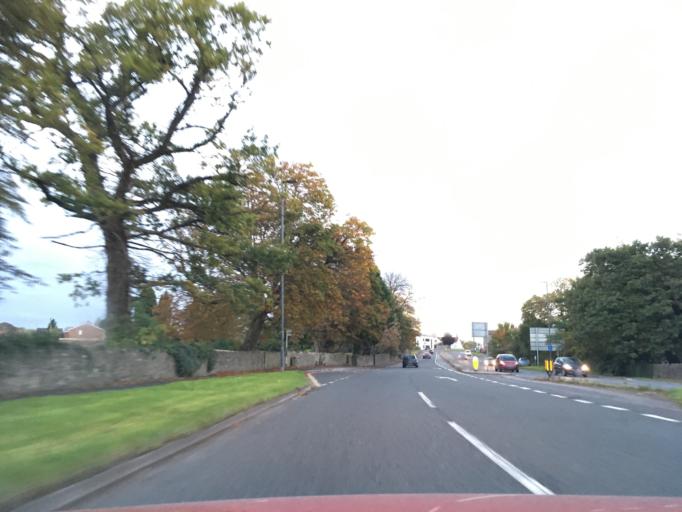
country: GB
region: England
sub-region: South Gloucestershire
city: Almondsbury
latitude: 51.5493
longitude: -2.5698
